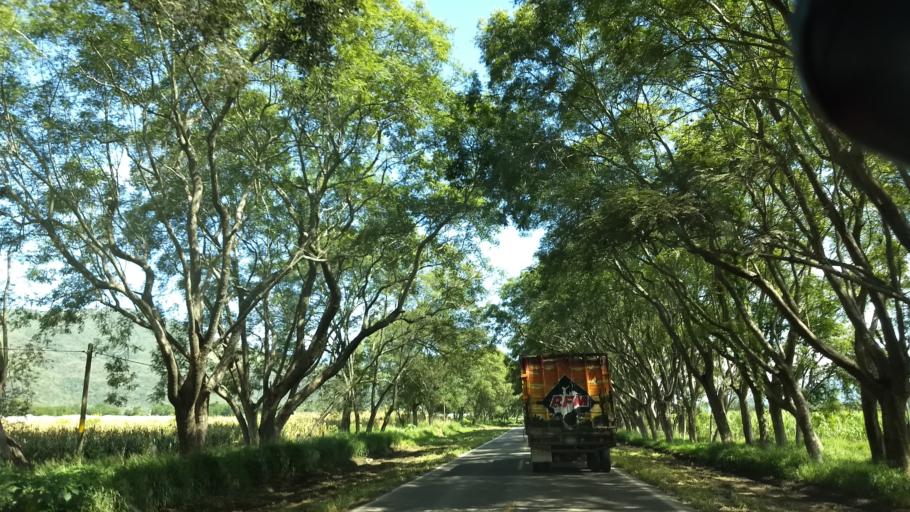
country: MX
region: Jalisco
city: Tuxpan
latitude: 19.5331
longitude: -103.4170
